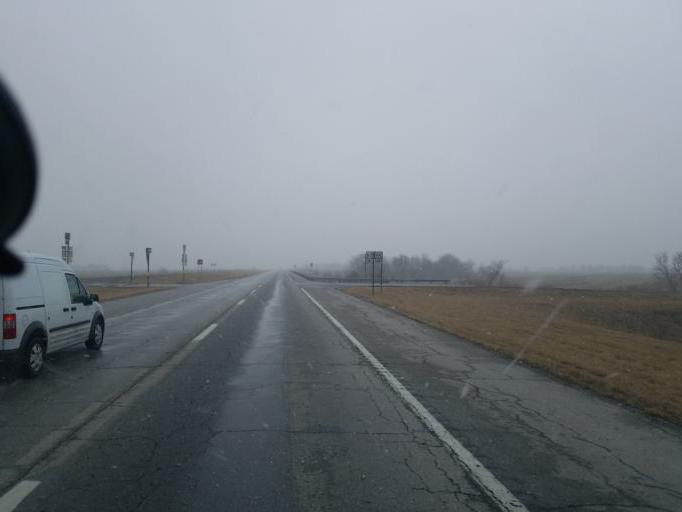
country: US
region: Missouri
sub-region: Macon County
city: La Plata
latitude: 39.9849
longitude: -92.4760
